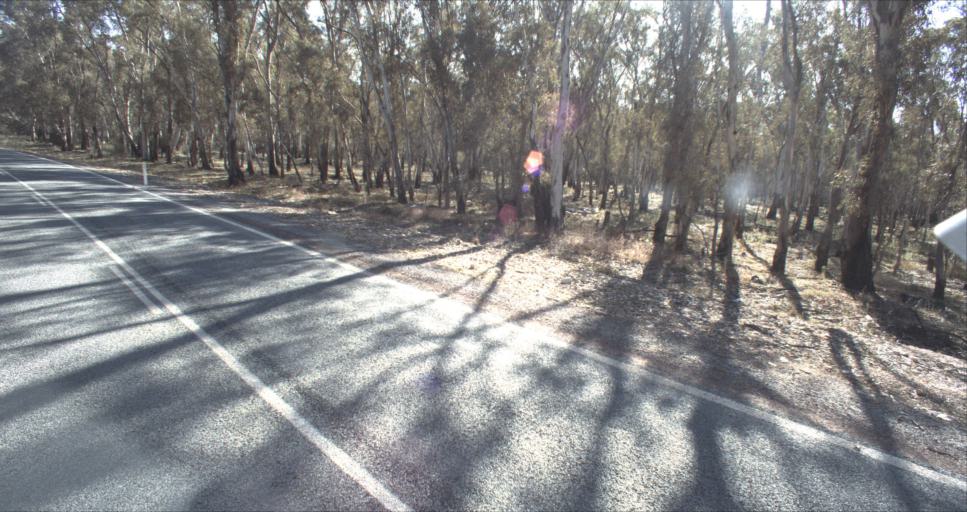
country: AU
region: New South Wales
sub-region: Leeton
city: Leeton
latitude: -34.6250
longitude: 146.3802
